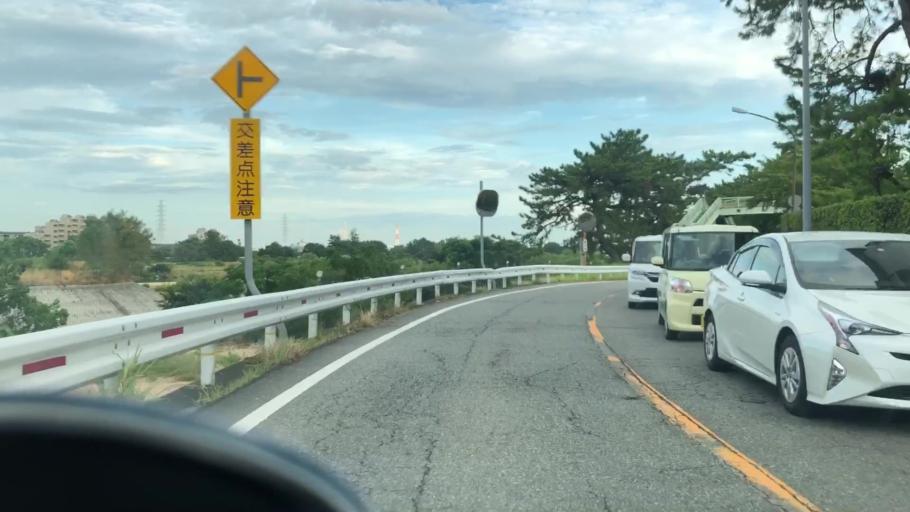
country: JP
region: Hyogo
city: Takarazuka
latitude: 34.7733
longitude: 135.3717
